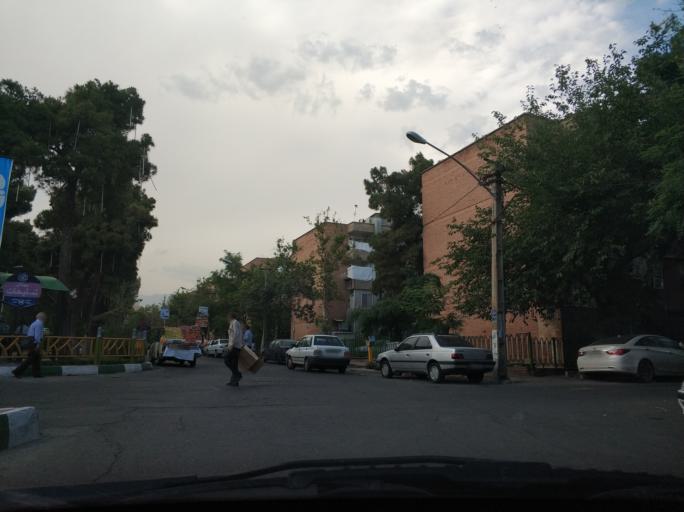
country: IR
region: Tehran
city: Tehran
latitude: 35.7179
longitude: 51.4744
